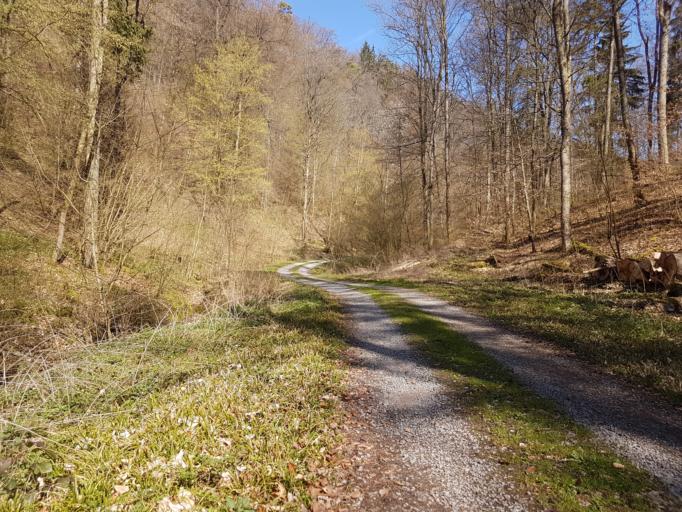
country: DE
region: Baden-Wuerttemberg
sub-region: Regierungsbezirk Stuttgart
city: Jagsthausen
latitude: 49.3339
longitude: 9.4886
